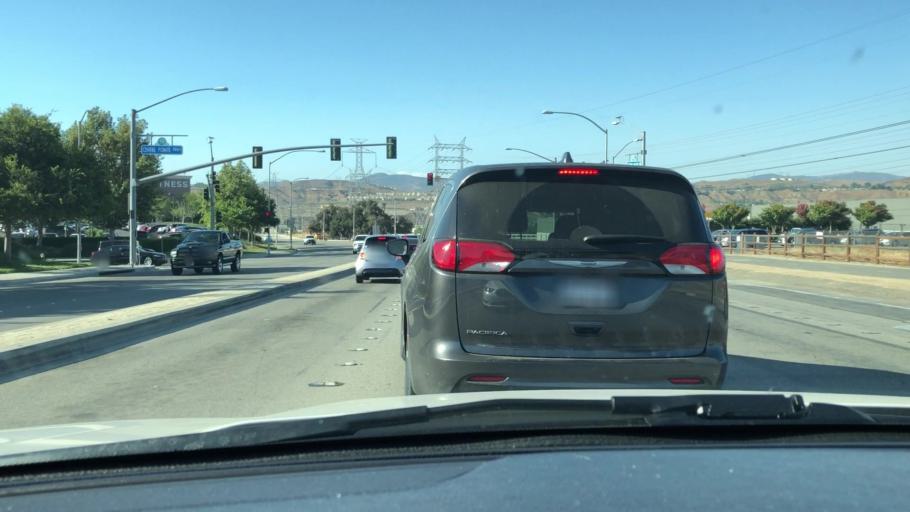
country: US
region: California
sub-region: Los Angeles County
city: Santa Clarita
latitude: 34.4121
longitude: -118.5023
